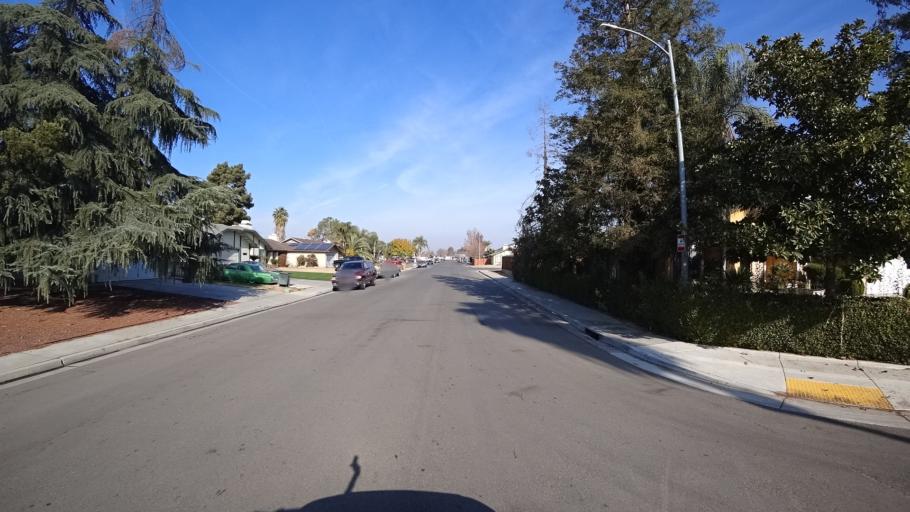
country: US
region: California
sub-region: Kern County
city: Greenfield
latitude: 35.3039
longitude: -119.0274
